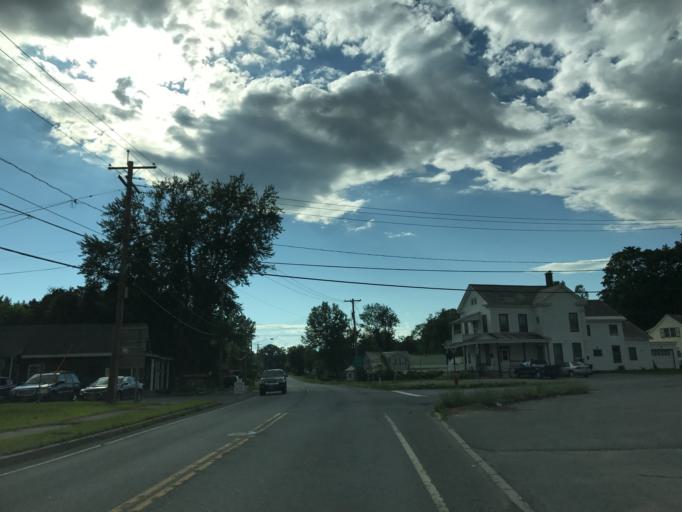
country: US
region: New York
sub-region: Washington County
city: Hudson Falls
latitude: 43.3088
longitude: -73.5949
